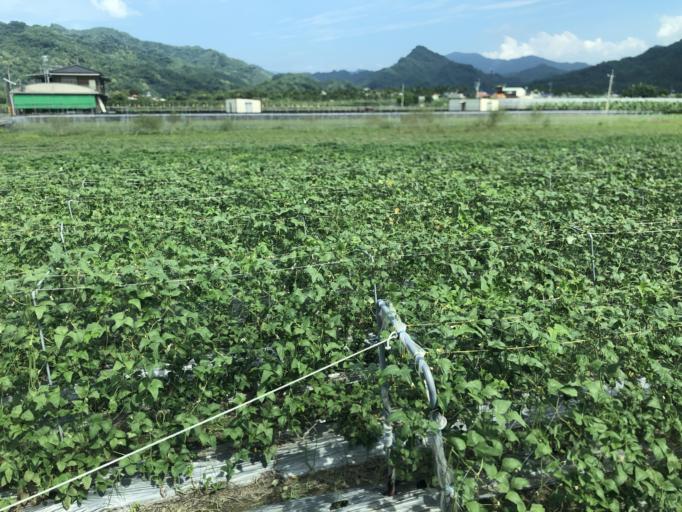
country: TW
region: Taiwan
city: Yujing
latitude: 22.9129
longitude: 120.5722
